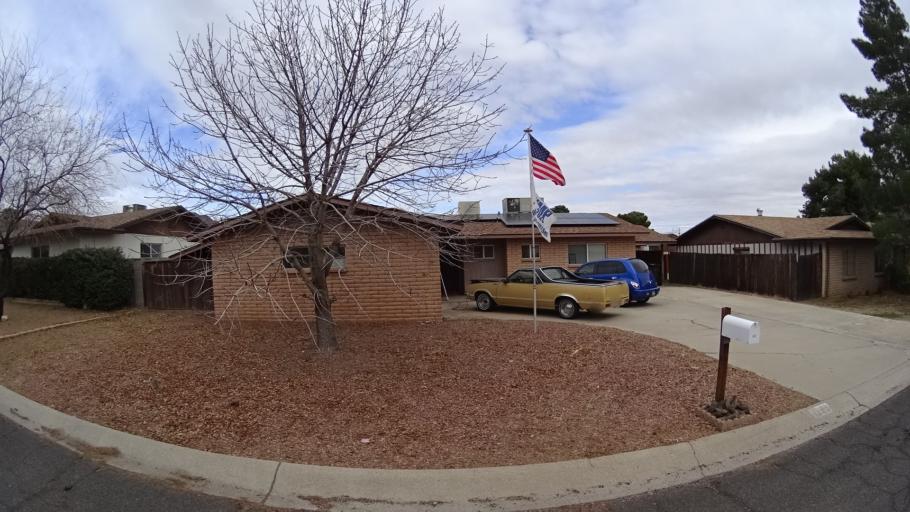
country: US
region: Arizona
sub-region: Mohave County
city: New Kingman-Butler
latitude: 35.2379
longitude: -114.0415
